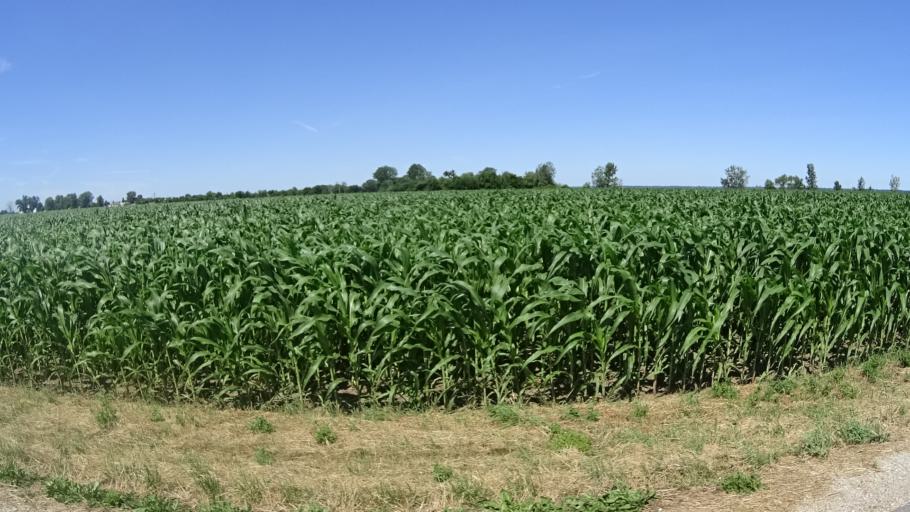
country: US
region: Ohio
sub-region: Ottawa County
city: Port Clinton
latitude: 41.4408
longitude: -82.8528
